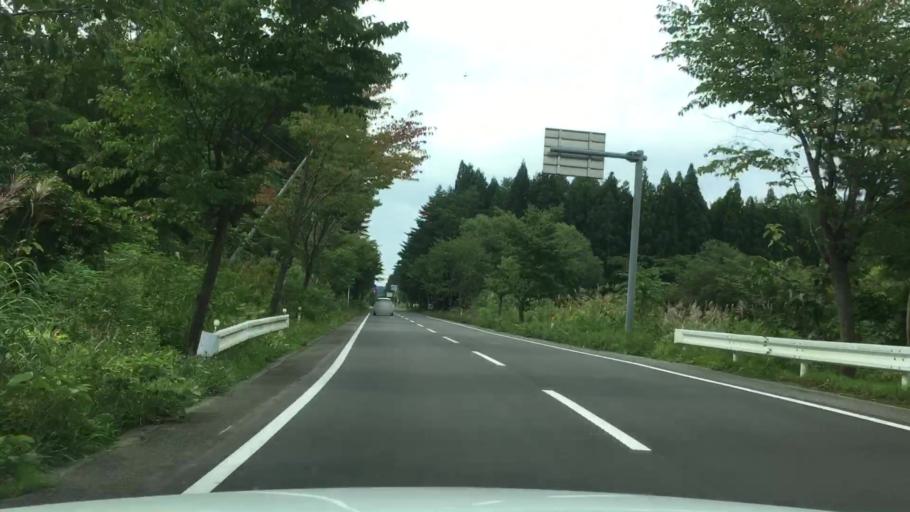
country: JP
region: Aomori
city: Shimokizukuri
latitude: 40.7107
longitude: 140.2806
